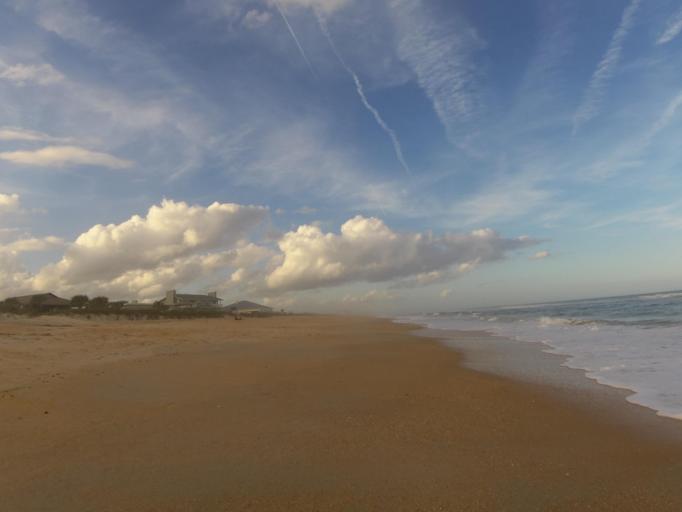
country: US
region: Florida
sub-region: Flagler County
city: Palm Coast
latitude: 29.6311
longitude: -81.1966
